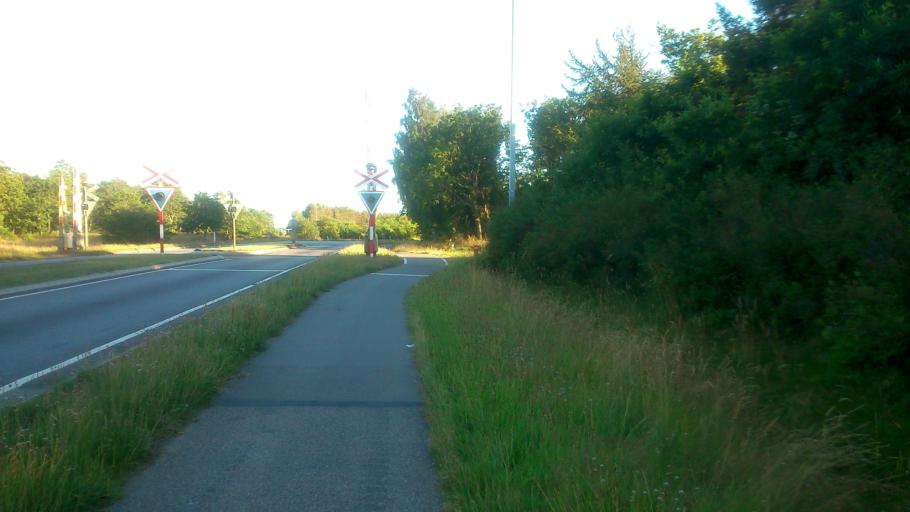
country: DK
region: Central Jutland
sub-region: Ringkobing-Skjern Kommune
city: Skjern
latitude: 55.9413
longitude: 8.5178
